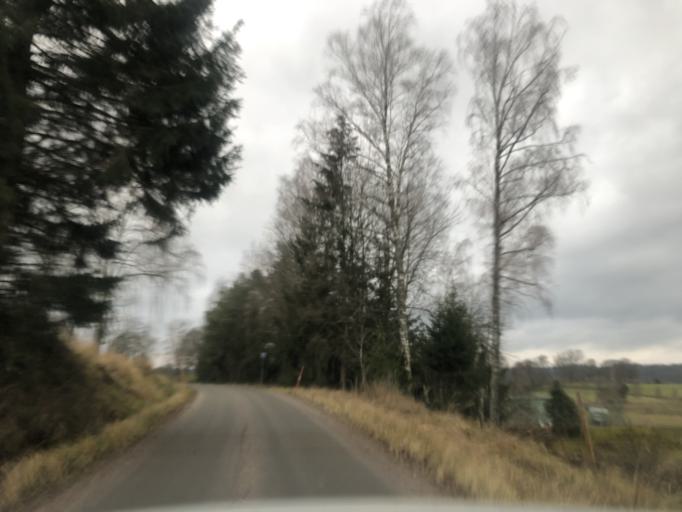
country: SE
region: Vaestra Goetaland
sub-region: Ulricehamns Kommun
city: Ulricehamn
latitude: 57.8873
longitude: 13.4650
